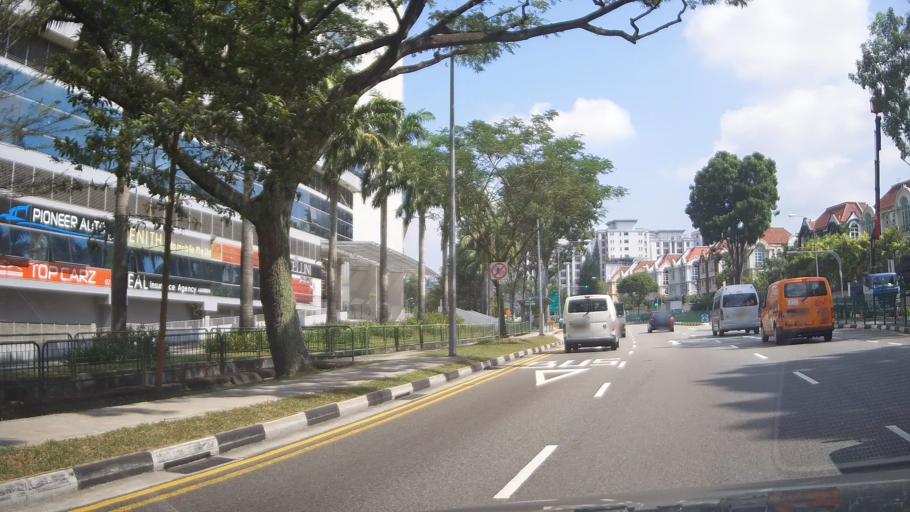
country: SG
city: Singapore
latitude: 1.3379
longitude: 103.7603
